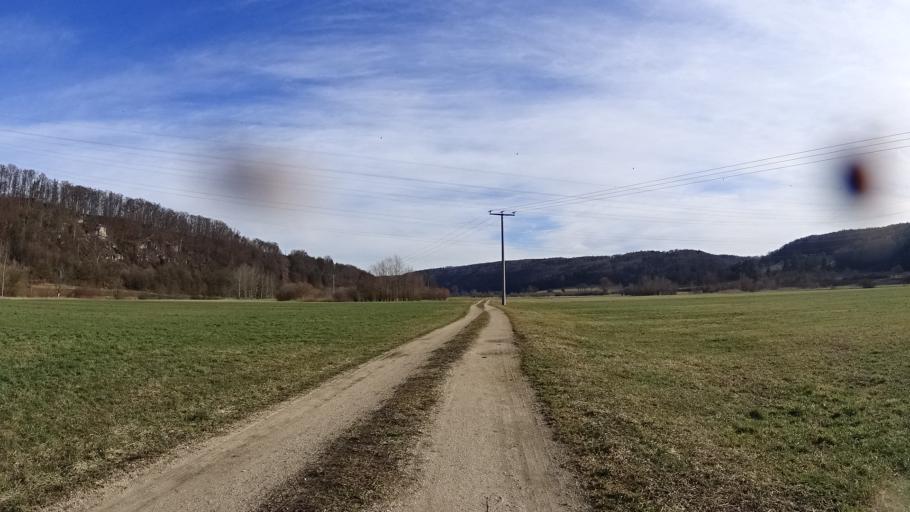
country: DE
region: Bavaria
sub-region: Upper Bavaria
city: Walting
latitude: 48.8983
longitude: 11.2800
